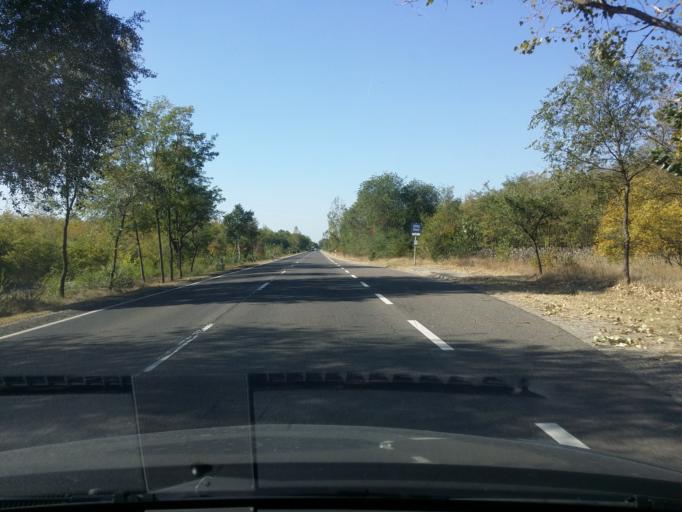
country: HU
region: Bacs-Kiskun
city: Nyarlorinc
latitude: 46.8637
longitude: 19.9211
